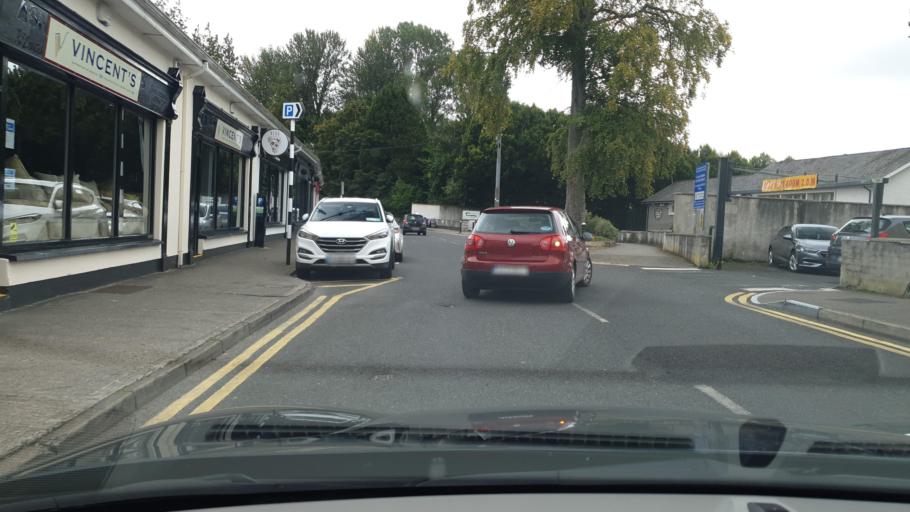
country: IE
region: Leinster
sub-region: Kildare
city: Naas
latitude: 53.2188
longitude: -6.6605
